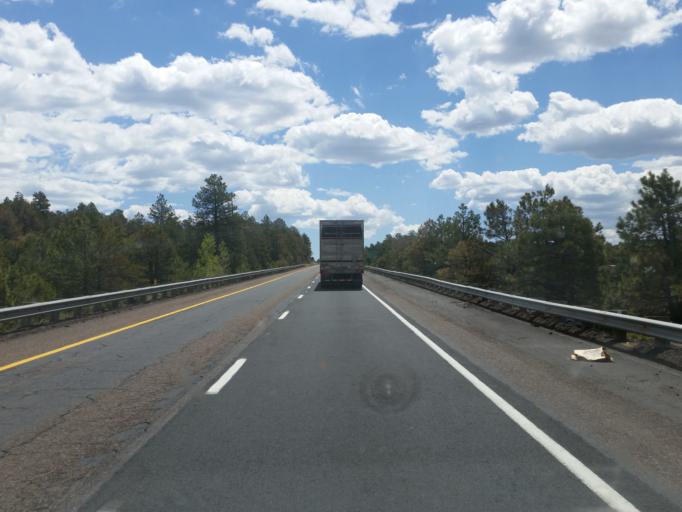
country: US
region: Arizona
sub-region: Coconino County
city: Parks
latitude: 35.2548
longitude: -111.9186
